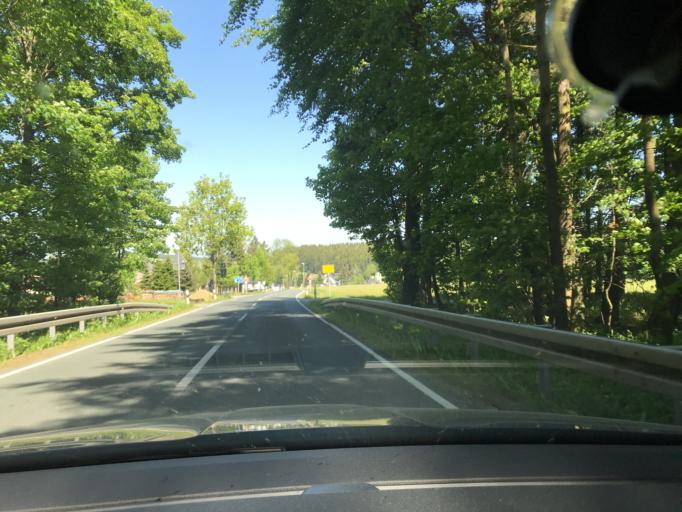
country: CZ
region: Ustecky
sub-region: Okres Chomutov
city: Vejprty
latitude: 50.4648
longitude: 12.9913
